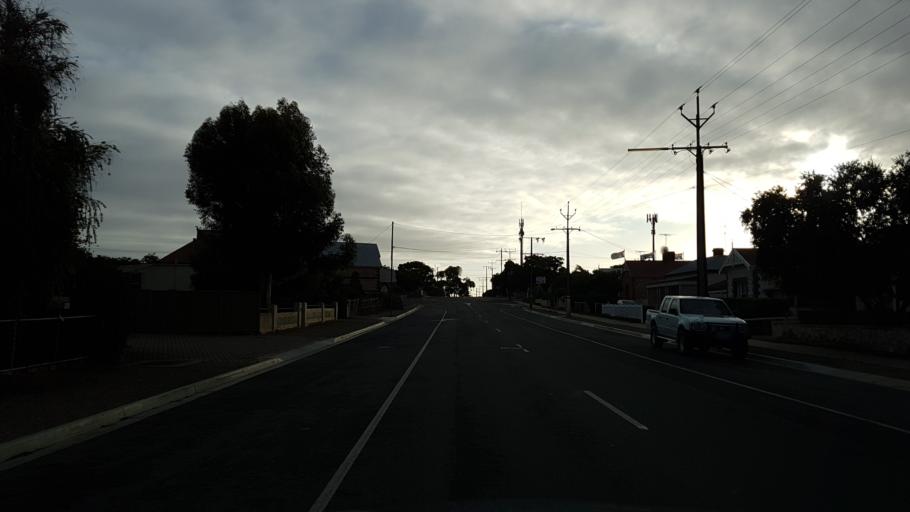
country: AU
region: South Australia
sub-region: Murray Bridge
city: Murray Bridge
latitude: -35.1203
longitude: 139.2694
